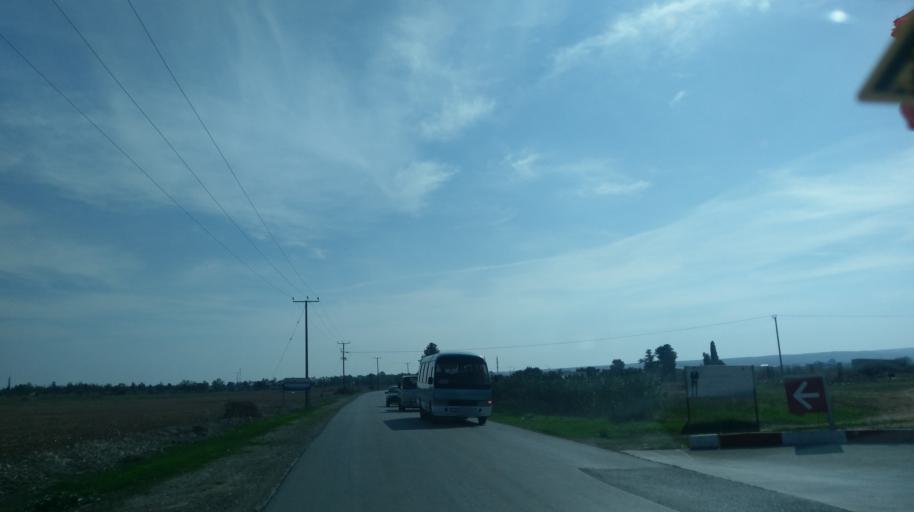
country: CY
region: Larnaka
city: Pergamos
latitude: 35.1215
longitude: 33.6683
